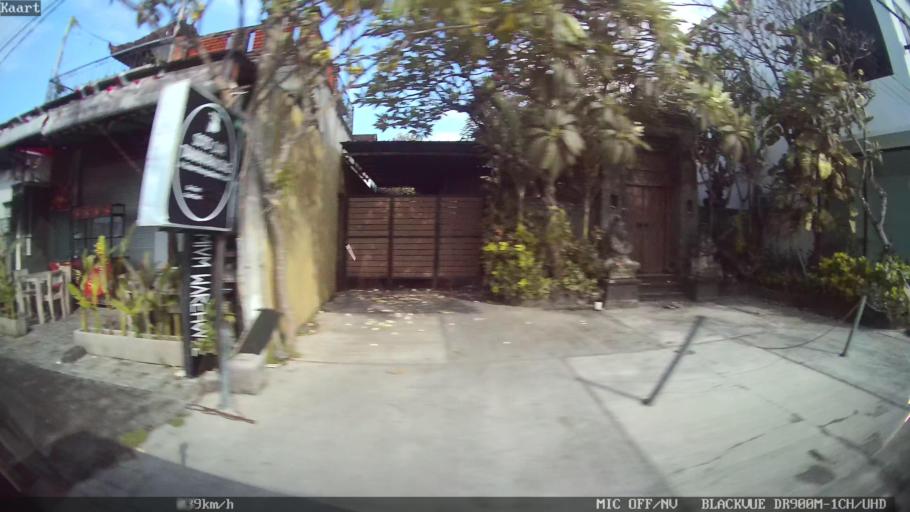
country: ID
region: Bali
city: Kuta
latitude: -8.7062
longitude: 115.1919
